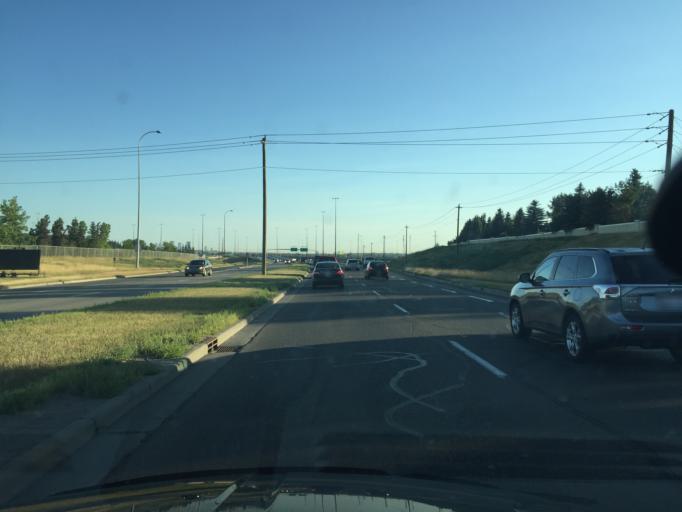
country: CA
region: Alberta
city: Calgary
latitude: 50.9457
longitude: -114.0261
